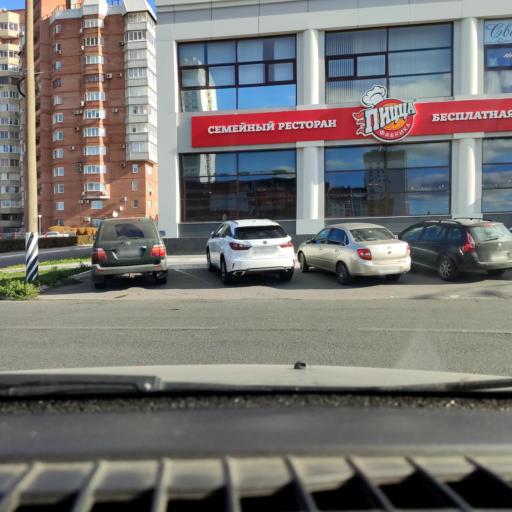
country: RU
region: Samara
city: Tol'yatti
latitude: 53.5005
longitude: 49.2747
